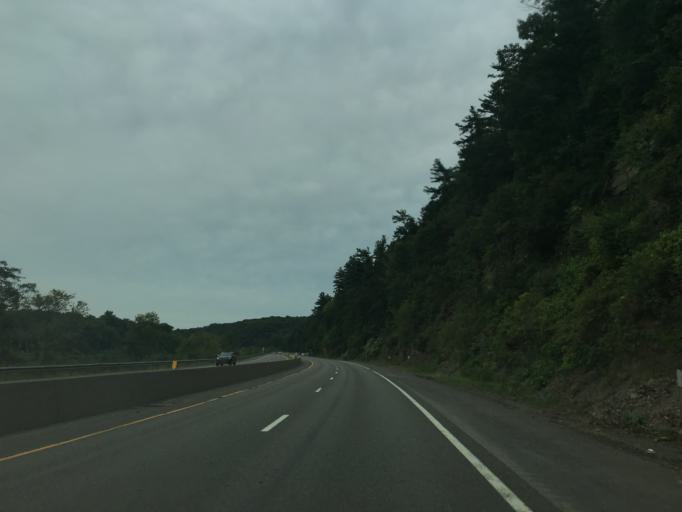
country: US
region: New York
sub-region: Broome County
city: Chenango Bridge
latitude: 42.1614
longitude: -75.8601
